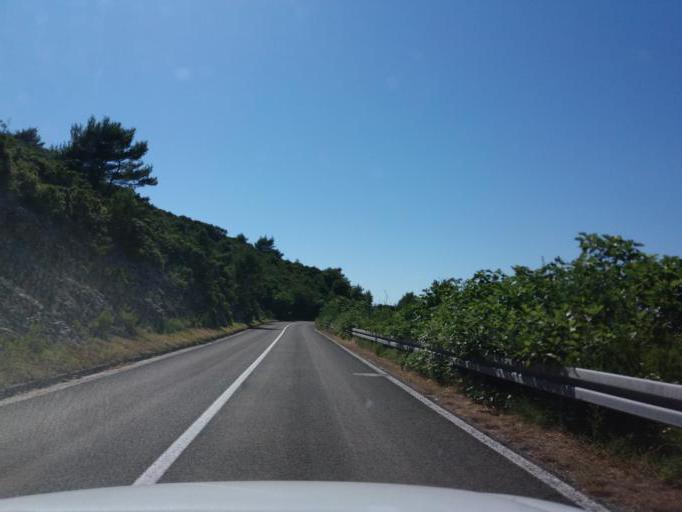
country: HR
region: Zadarska
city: Ugljan
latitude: 44.1194
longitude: 14.9203
